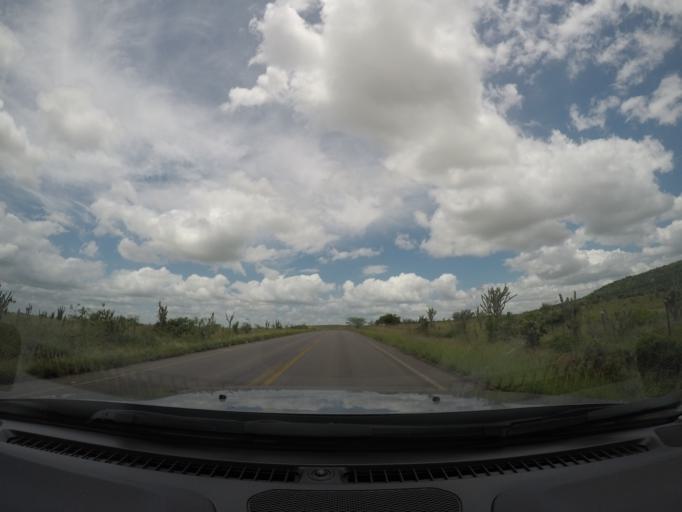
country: BR
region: Bahia
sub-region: Ipira
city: Ipira
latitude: -12.2623
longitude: -39.8293
